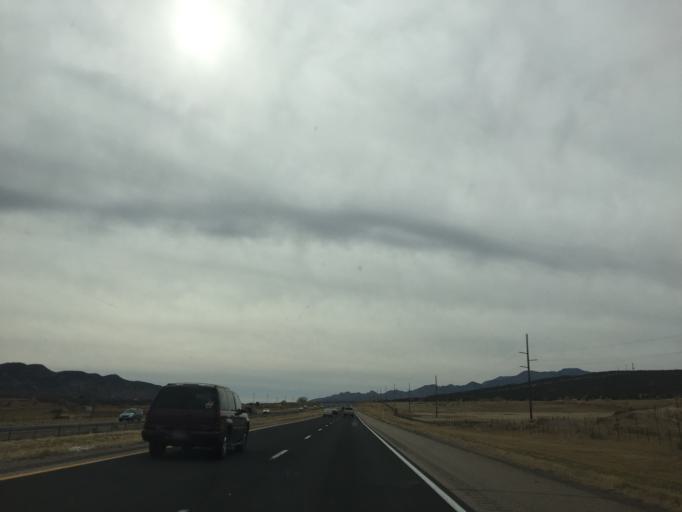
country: US
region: Utah
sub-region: Iron County
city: Cedar City
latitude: 37.5485
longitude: -113.1980
